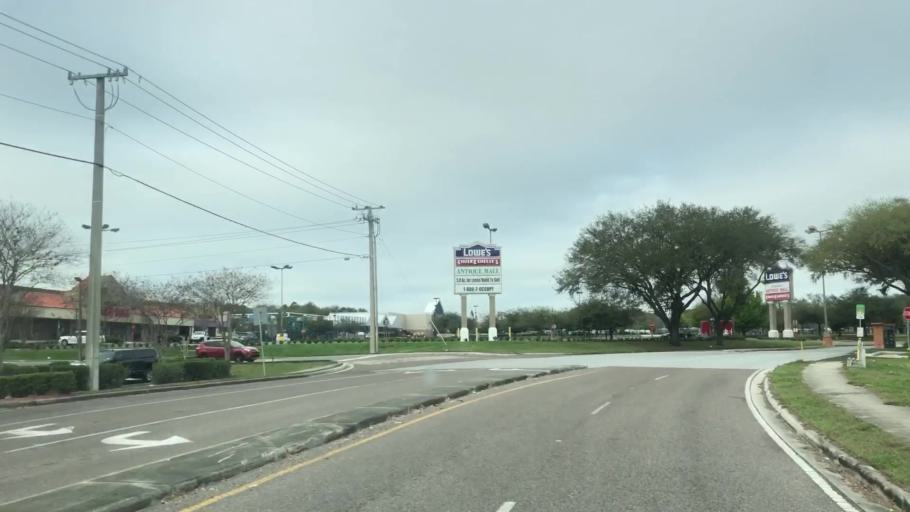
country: US
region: Florida
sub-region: Polk County
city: Gibsonia
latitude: 28.0880
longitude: -81.9732
